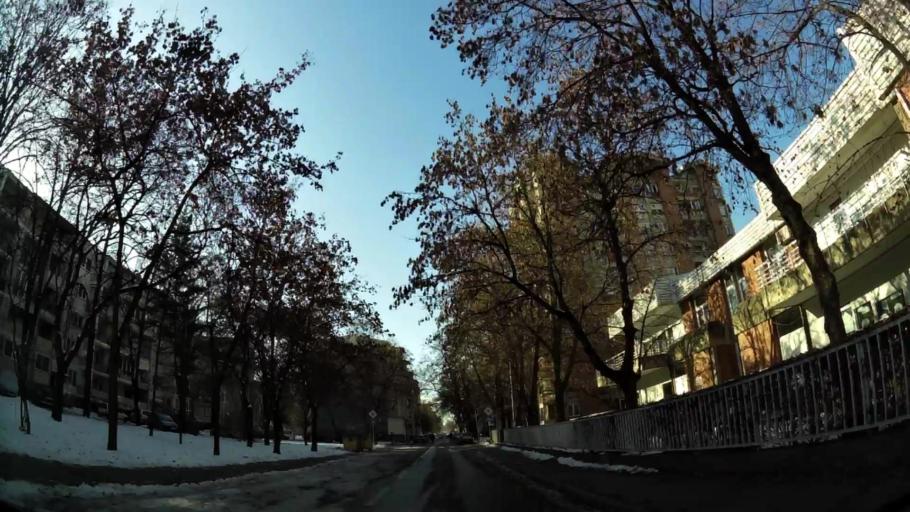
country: MK
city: Krushopek
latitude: 42.0075
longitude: 21.3868
